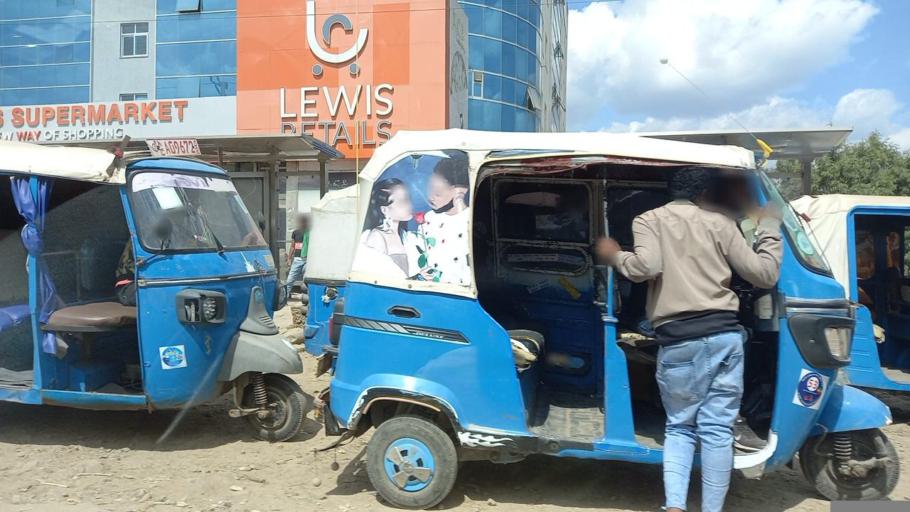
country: ET
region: Adis Abeba
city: Addis Ababa
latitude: 8.9484
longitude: 38.7325
